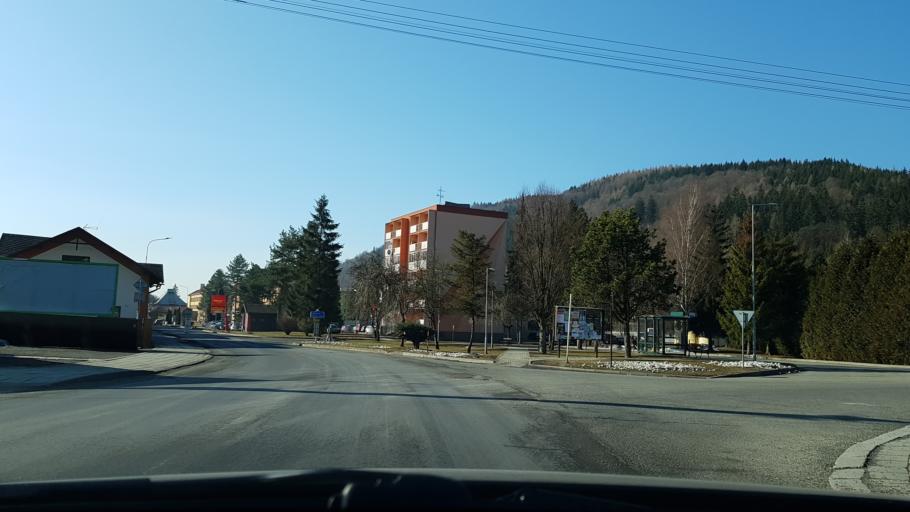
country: CZ
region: Olomoucky
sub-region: Okres Sumperk
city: Hanusovice
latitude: 50.0777
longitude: 16.9332
